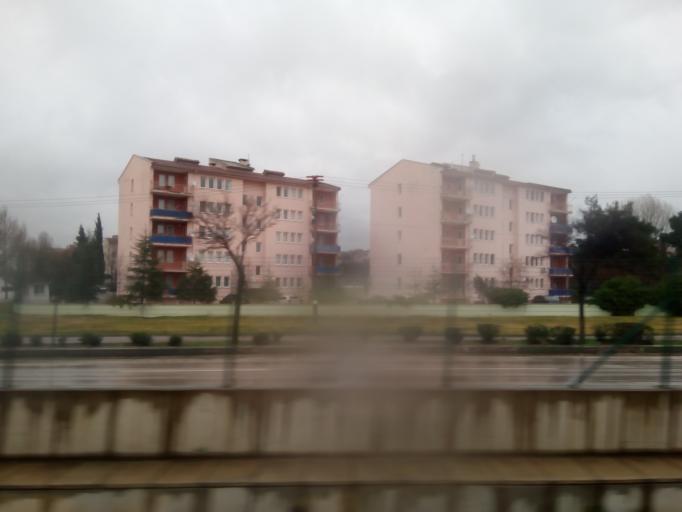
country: TR
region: Bursa
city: Niluefer
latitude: 40.2449
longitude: 28.9652
